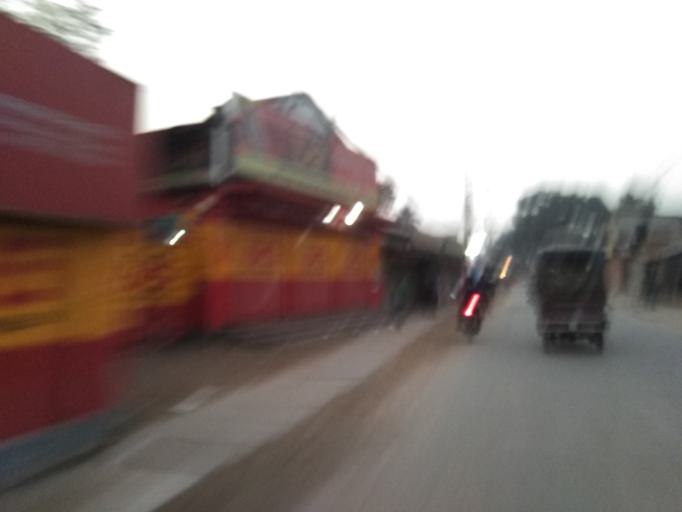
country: BD
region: Rangpur Division
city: Rangpur
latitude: 25.7408
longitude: 89.2522
